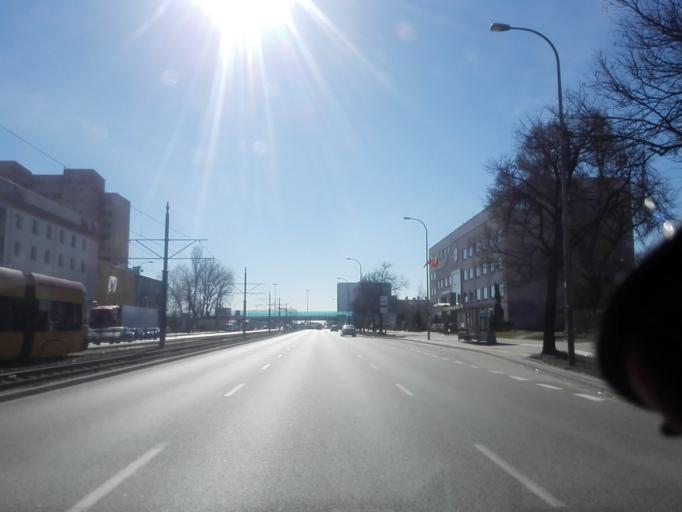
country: PL
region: Masovian Voivodeship
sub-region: Warszawa
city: Wlochy
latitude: 52.1931
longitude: 20.9606
